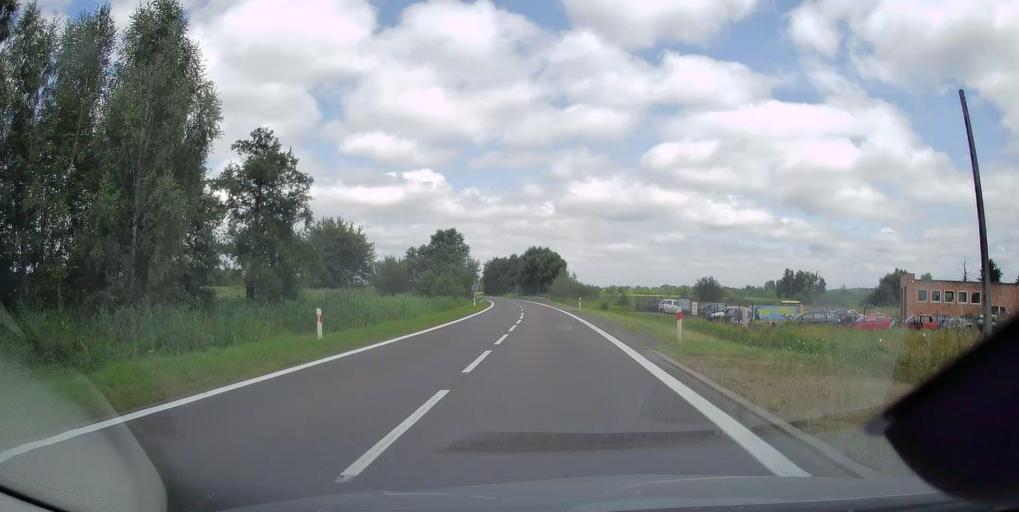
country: PL
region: Subcarpathian Voivodeship
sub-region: Powiat tarnobrzeski
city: Baranow Sandomierski
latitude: 50.4885
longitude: 21.5688
